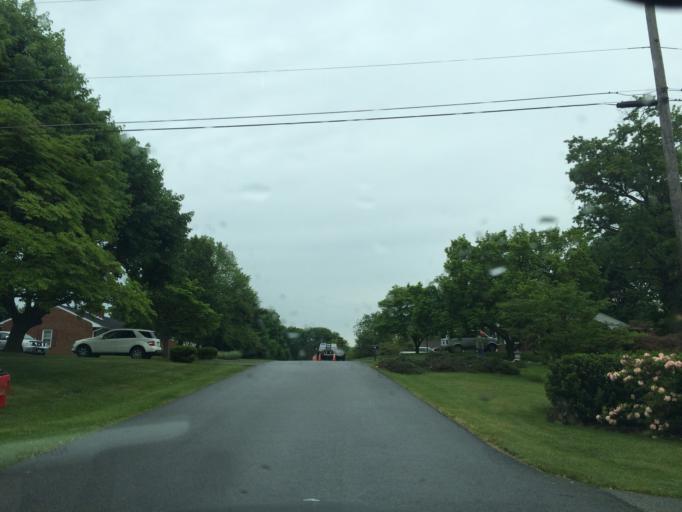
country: US
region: Maryland
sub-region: Washington County
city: Robinwood
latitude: 39.6160
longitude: -77.6875
